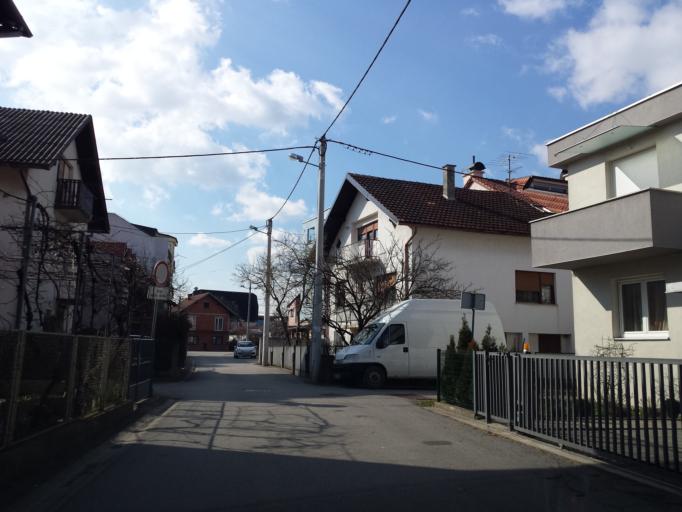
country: HR
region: Grad Zagreb
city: Jankomir
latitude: 45.7971
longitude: 15.9238
